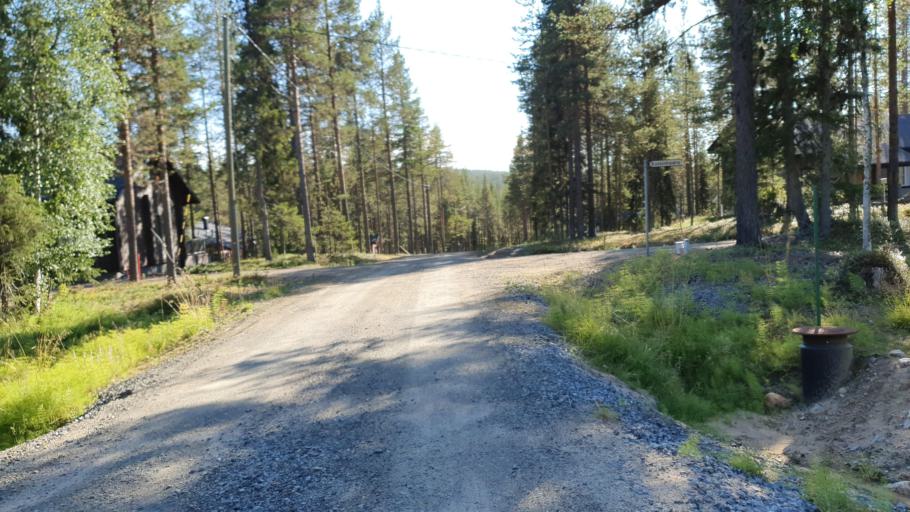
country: FI
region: Lapland
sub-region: Tunturi-Lappi
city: Kolari
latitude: 67.6058
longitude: 24.2059
